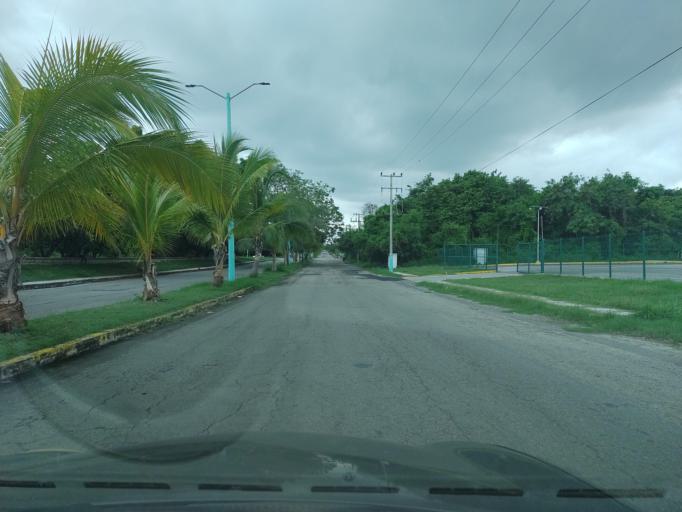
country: MX
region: Quintana Roo
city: Chetumal
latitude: 18.5237
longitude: -88.2737
